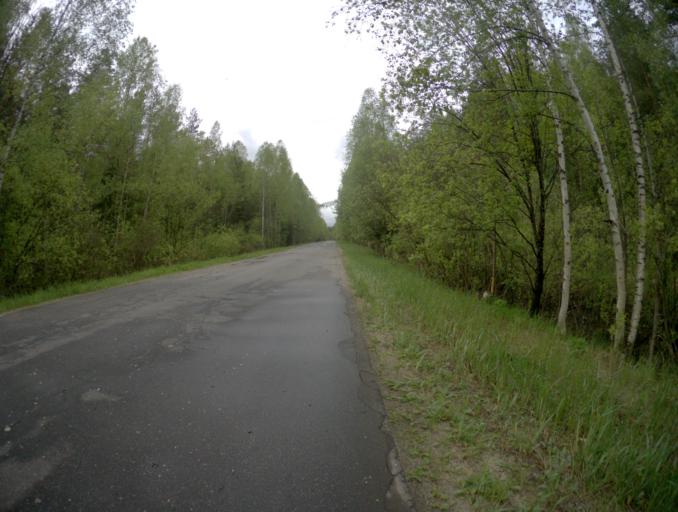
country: RU
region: Vladimir
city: Zolotkovo
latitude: 55.3469
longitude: 40.9671
